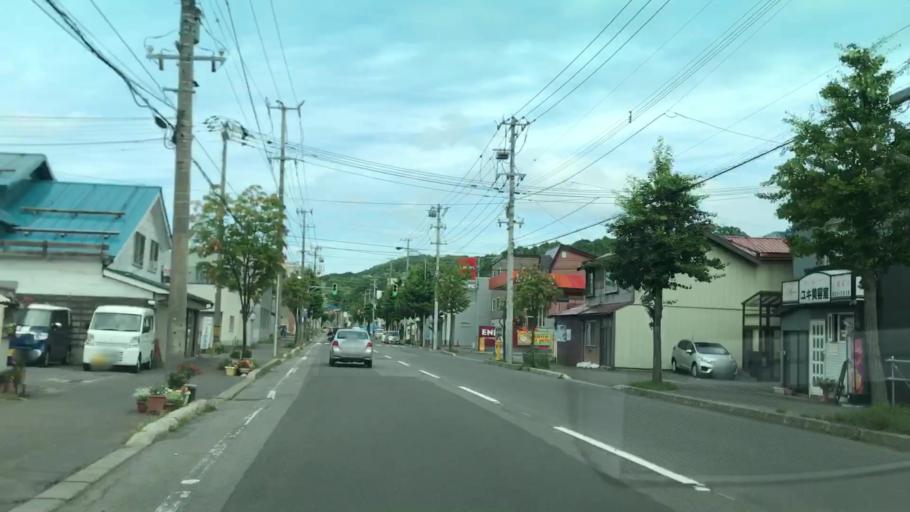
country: JP
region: Hokkaido
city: Otaru
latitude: 43.2065
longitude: 140.9834
